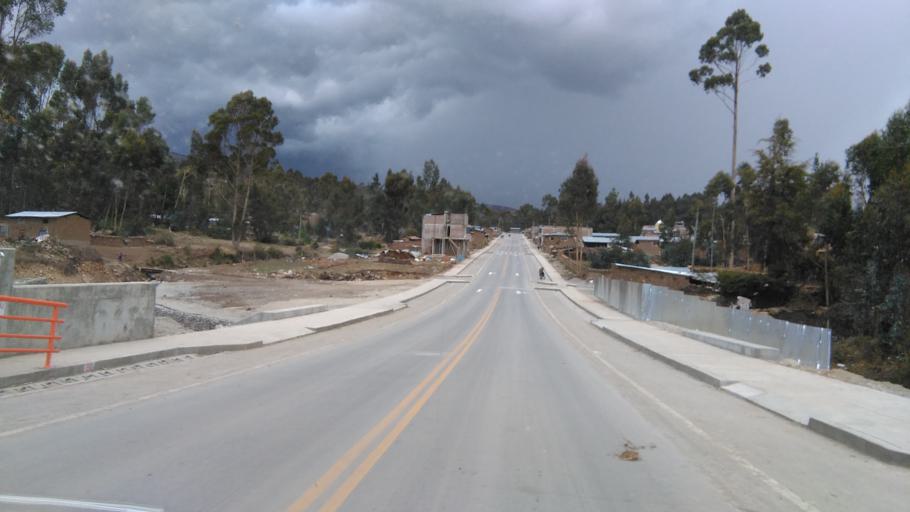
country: PE
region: Apurimac
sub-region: Provincia de Andahuaylas
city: San Jeronimo
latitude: -13.7308
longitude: -73.3514
